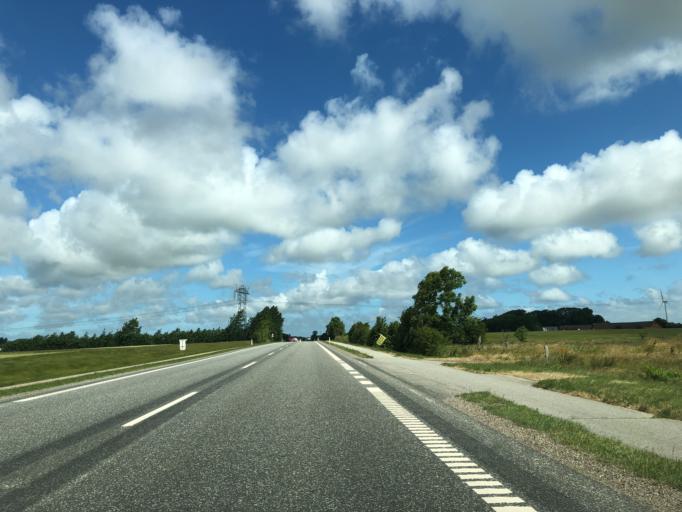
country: DK
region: Central Jutland
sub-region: Holstebro Kommune
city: Holstebro
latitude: 56.3987
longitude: 8.6081
